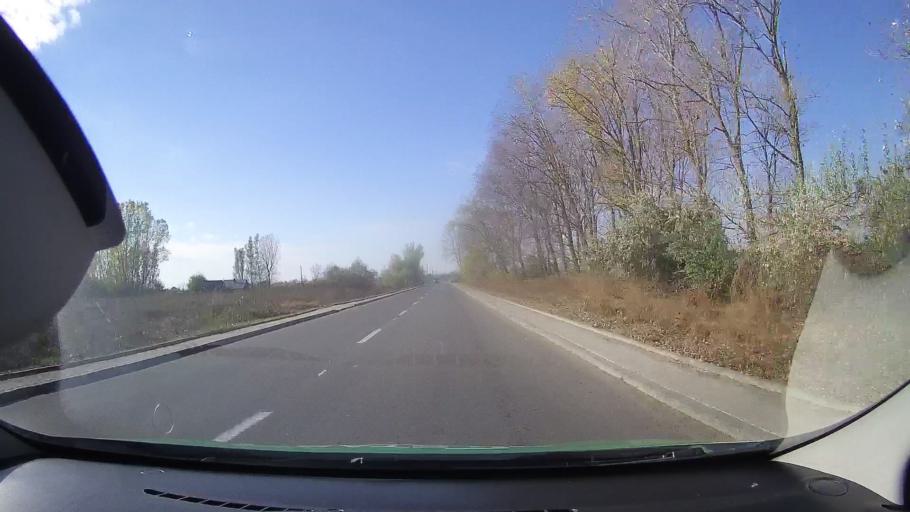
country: RO
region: Tulcea
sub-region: Comuna Mahmudia
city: Mahmudia
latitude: 45.0113
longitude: 29.0670
